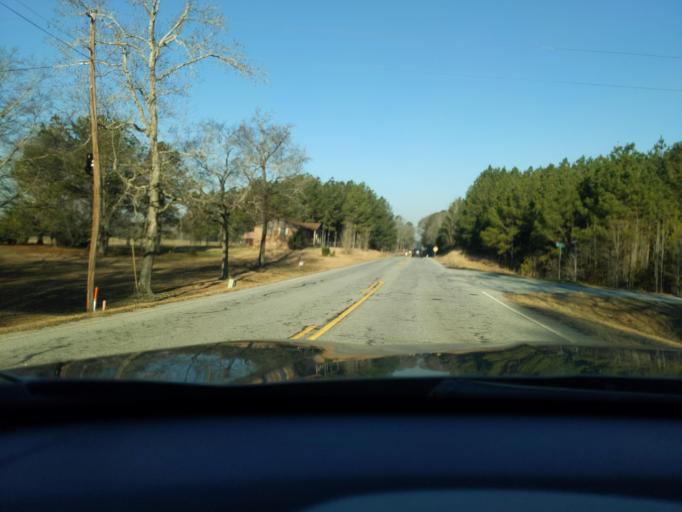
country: US
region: South Carolina
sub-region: Newberry County
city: Newberry
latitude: 34.2138
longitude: -81.7081
